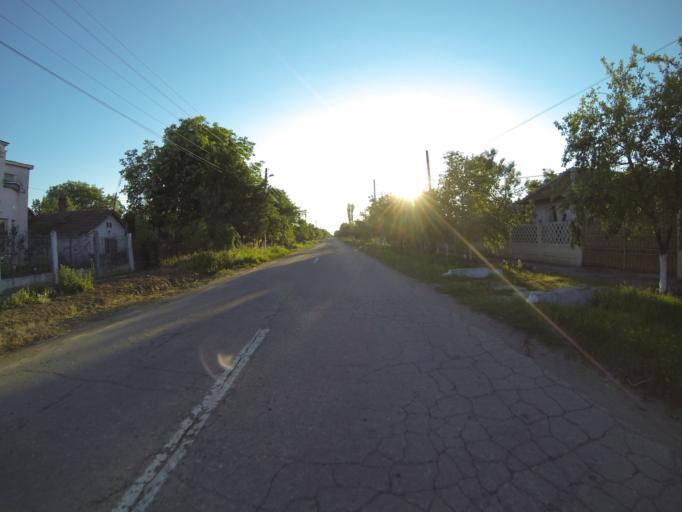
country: RO
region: Dolj
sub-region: Comuna Caloparu
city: Calopar
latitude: 44.1648
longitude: 23.7521
